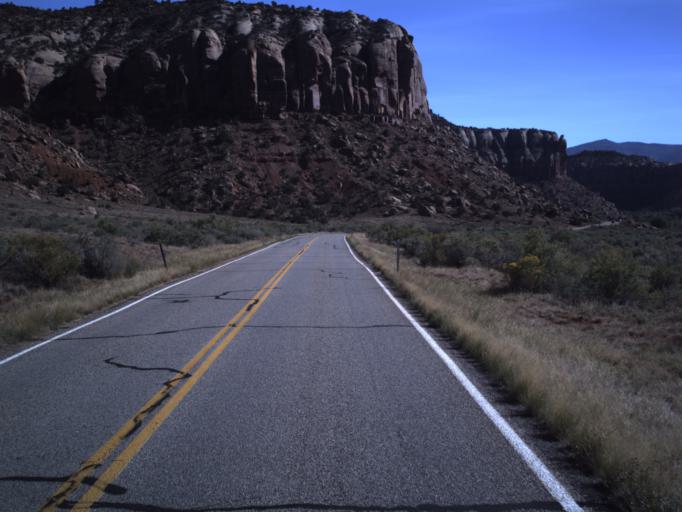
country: US
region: Utah
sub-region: San Juan County
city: Monticello
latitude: 38.0535
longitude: -109.5532
